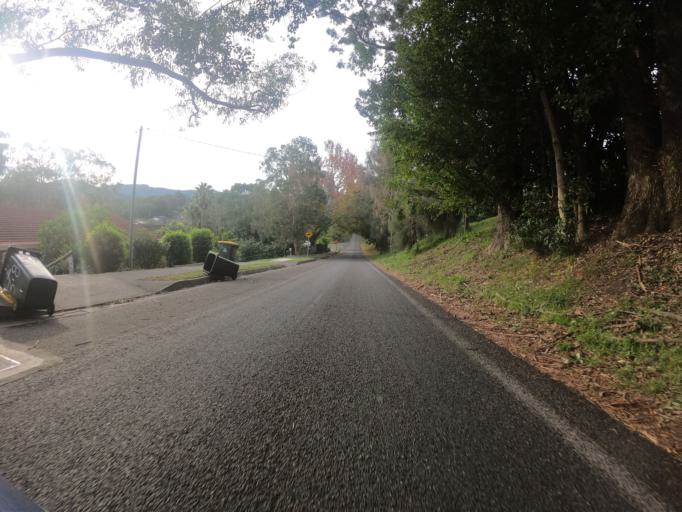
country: AU
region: New South Wales
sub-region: Wollongong
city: Mount Keira
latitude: -34.4314
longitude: 150.8533
